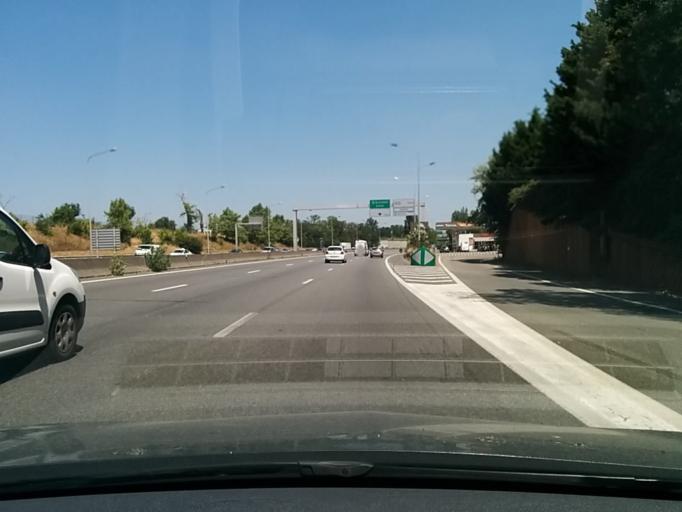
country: FR
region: Midi-Pyrenees
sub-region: Departement de la Haute-Garonne
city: Blagnac
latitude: 43.5993
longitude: 1.3976
